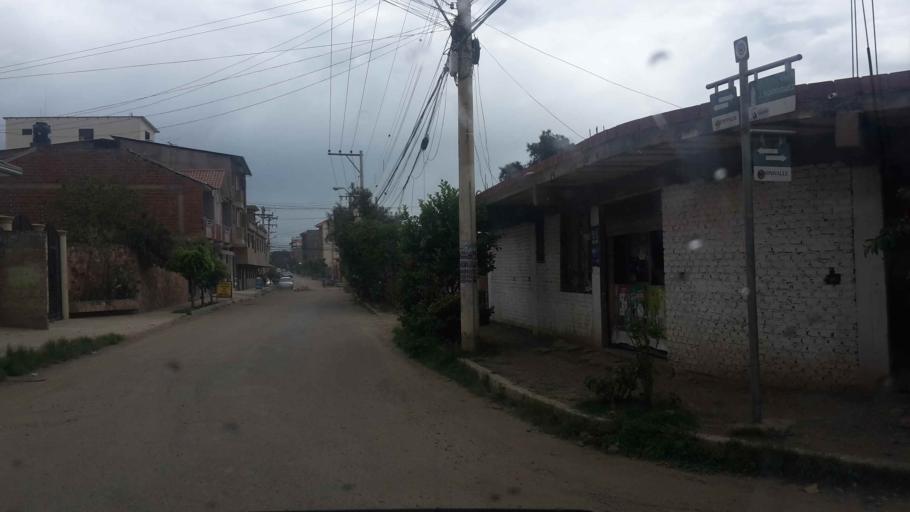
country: BO
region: Cochabamba
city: Cochabamba
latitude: -17.3394
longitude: -66.2229
